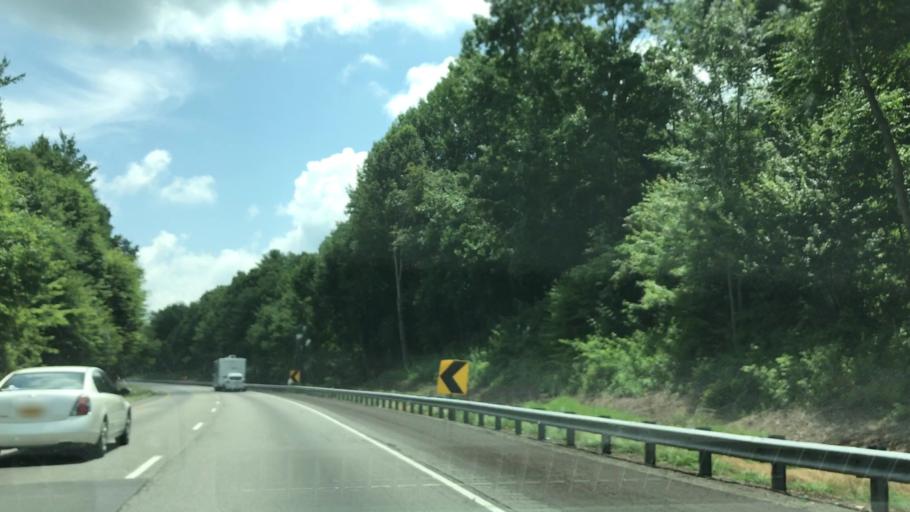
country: US
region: Virginia
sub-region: Carroll County
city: Woodlawn
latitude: 36.8100
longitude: -80.8551
